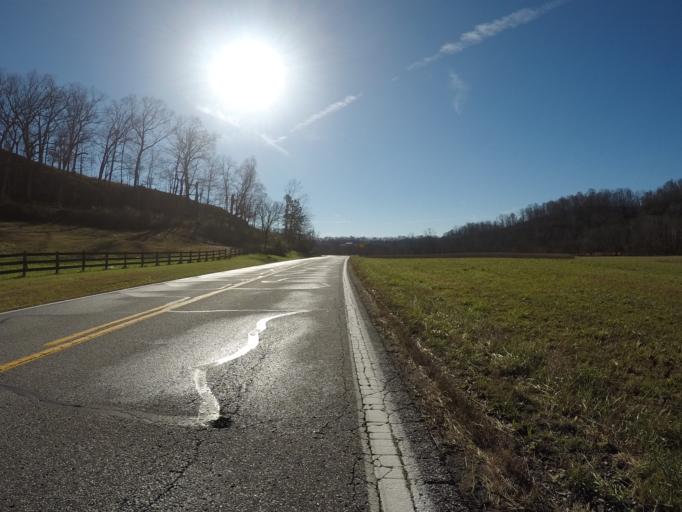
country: US
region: West Virginia
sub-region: Cabell County
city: Huntington
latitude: 38.4807
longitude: -82.4464
